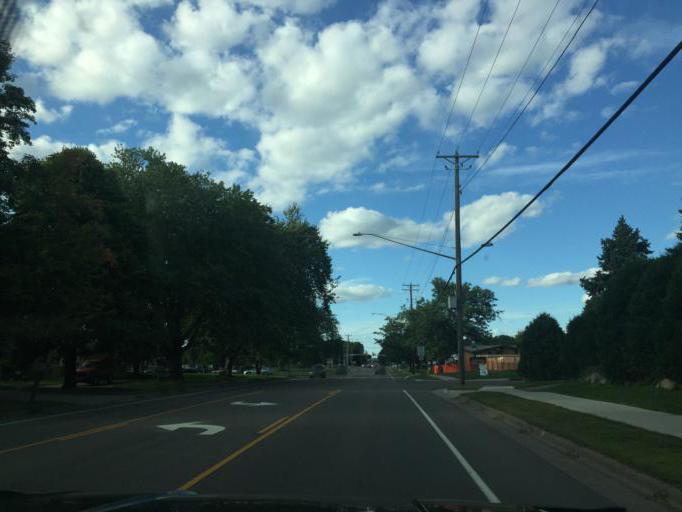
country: US
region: Minnesota
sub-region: Ramsey County
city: Roseville
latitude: 45.0038
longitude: -93.1463
